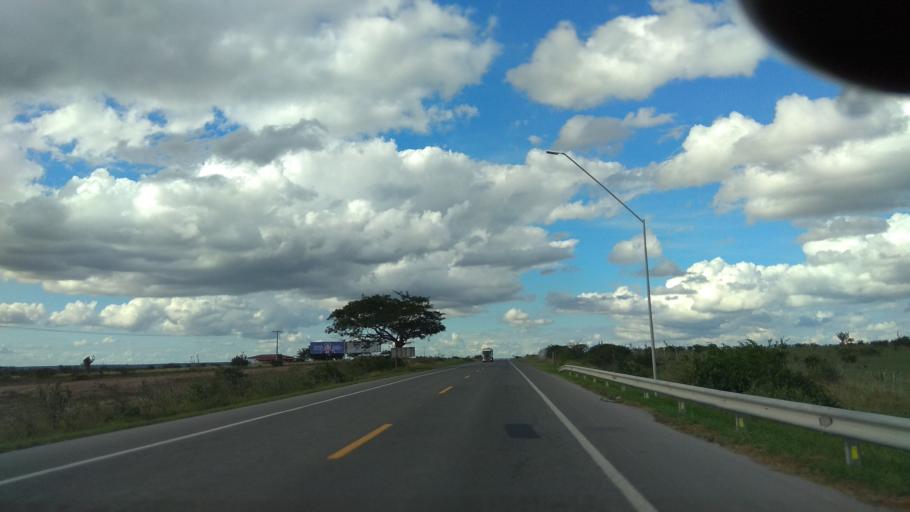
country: BR
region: Bahia
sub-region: Castro Alves
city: Castro Alves
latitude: -12.6086
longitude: -39.5603
